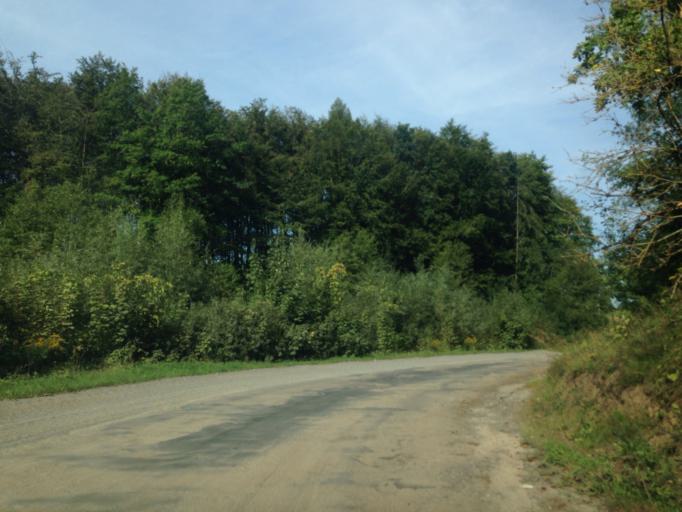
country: PL
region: Kujawsko-Pomorskie
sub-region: Powiat golubsko-dobrzynski
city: Golub-Dobrzyn
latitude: 53.1133
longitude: 19.0396
